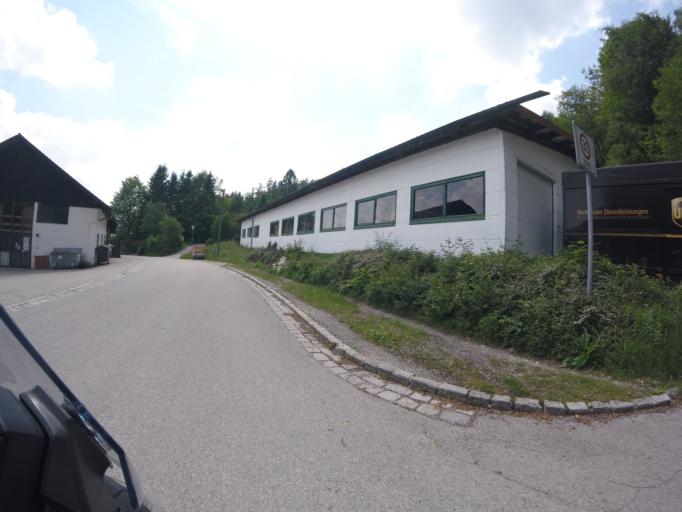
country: DE
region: Bavaria
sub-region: Upper Bavaria
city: Eurasburg
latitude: 47.8615
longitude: 11.4032
